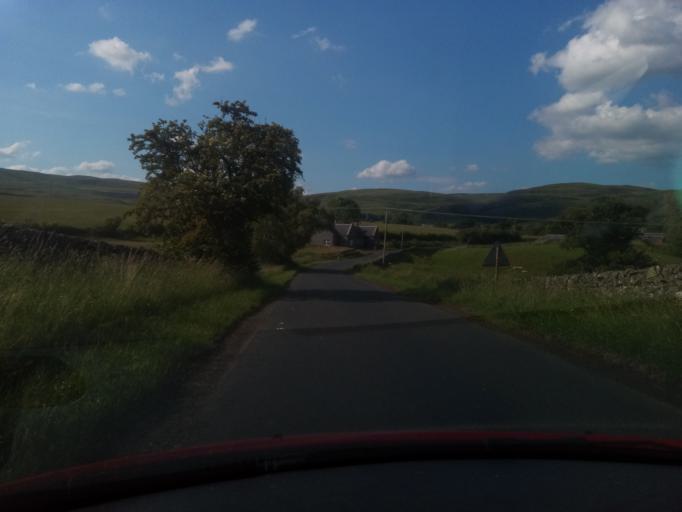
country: GB
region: Scotland
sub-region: The Scottish Borders
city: Innerleithen
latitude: 55.5018
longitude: -2.9834
